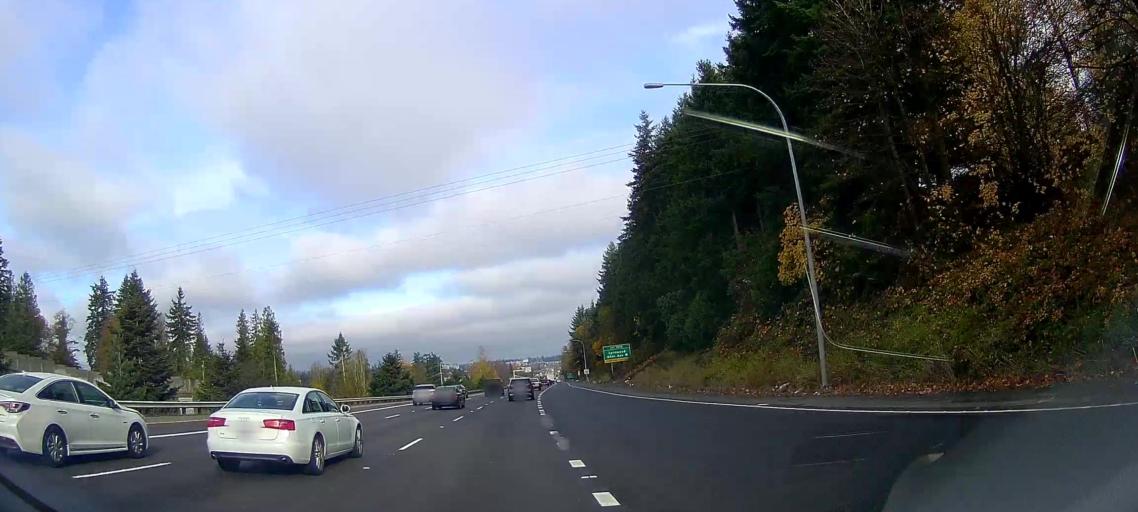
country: US
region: Washington
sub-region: Snohomish County
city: Mountlake Terrace
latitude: 47.8032
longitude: -122.3107
